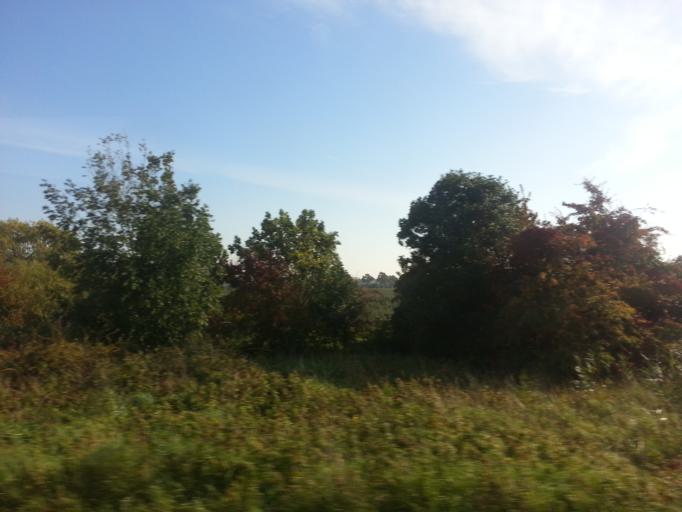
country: NL
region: Gelderland
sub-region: Gemeente Neerijnen
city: Neerijnen
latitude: 51.8366
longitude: 5.2581
